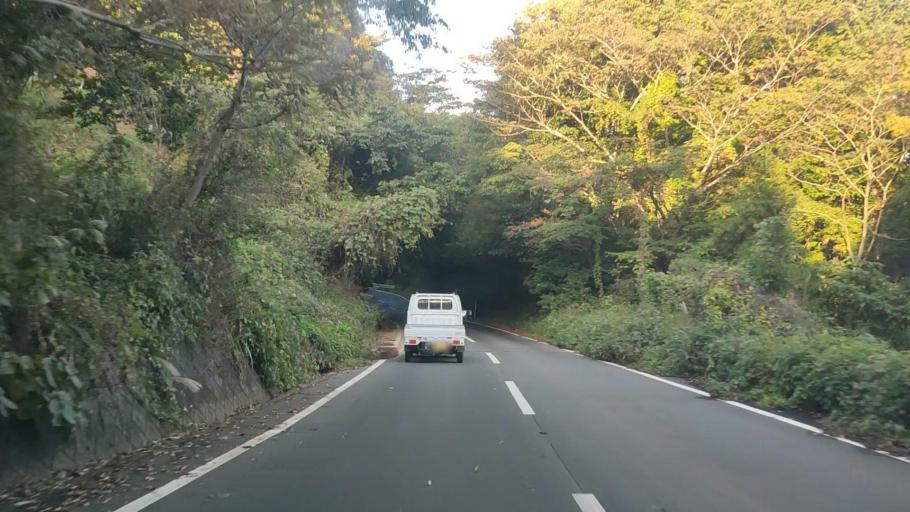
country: JP
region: Shizuoka
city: Mishima
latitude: 35.1312
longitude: 138.9758
